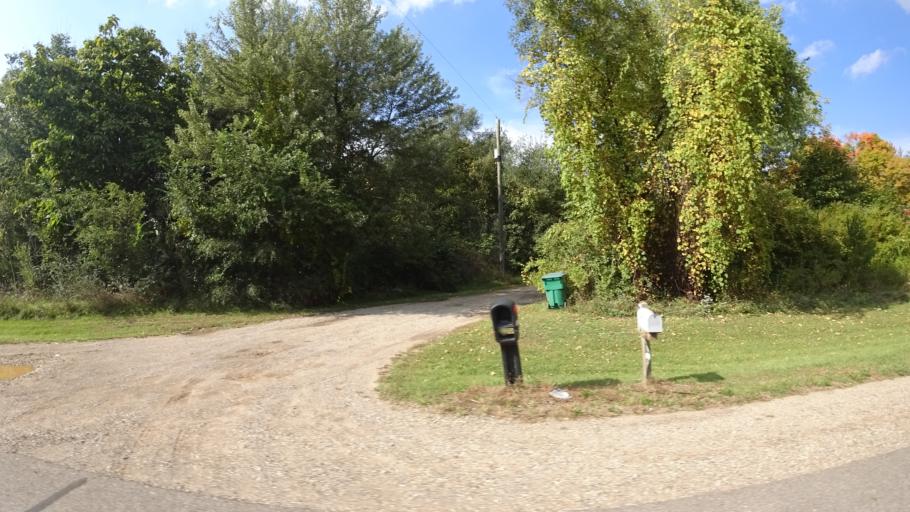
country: US
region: Michigan
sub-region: Saint Joseph County
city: Three Rivers
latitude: 41.9590
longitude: -85.5804
